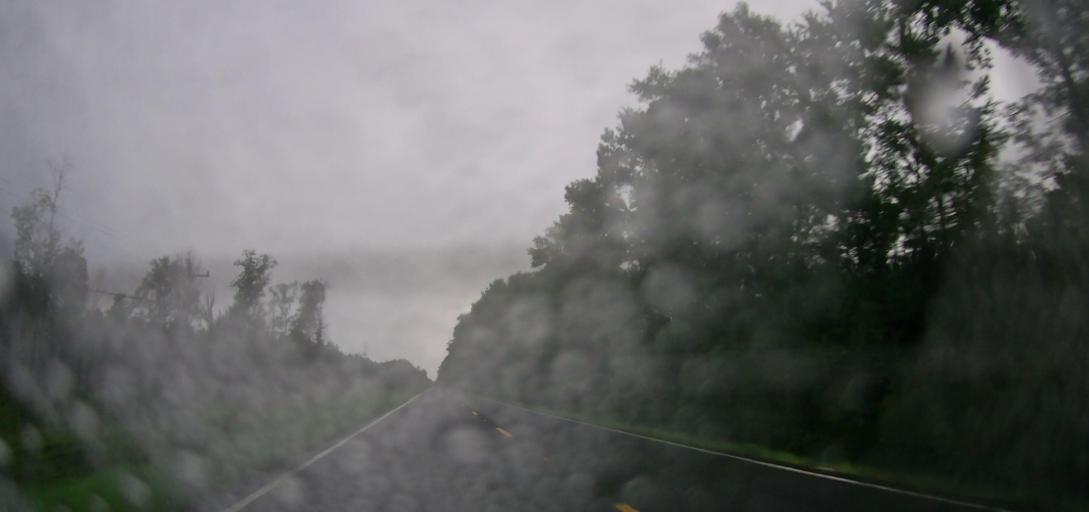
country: US
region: Georgia
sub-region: Glynn County
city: Dock Junction
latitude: 31.2688
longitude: -81.6396
